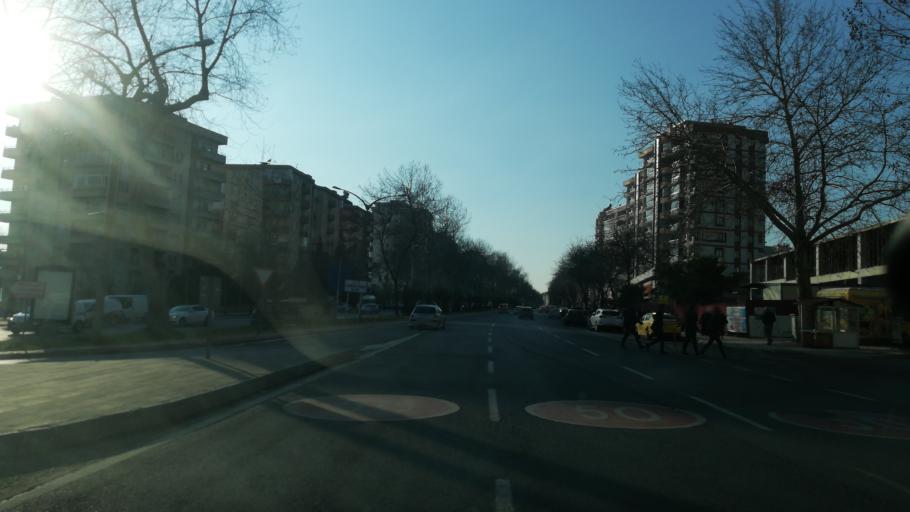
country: TR
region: Kahramanmaras
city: Kahramanmaras
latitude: 37.5867
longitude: 36.8976
